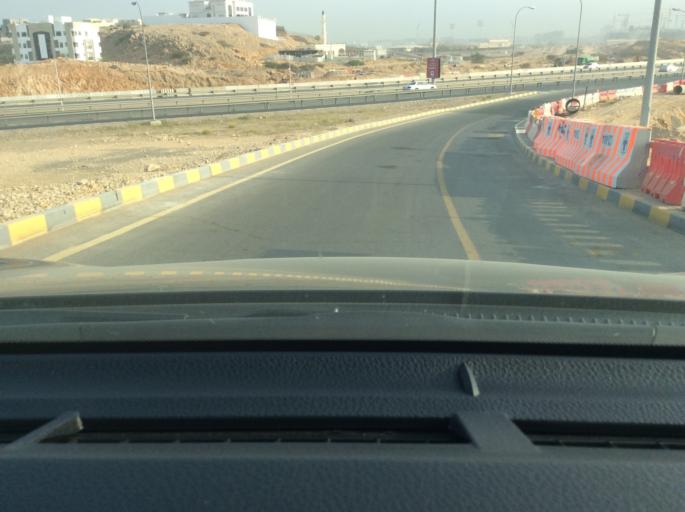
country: OM
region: Muhafazat Masqat
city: Bawshar
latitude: 23.5628
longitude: 58.3885
